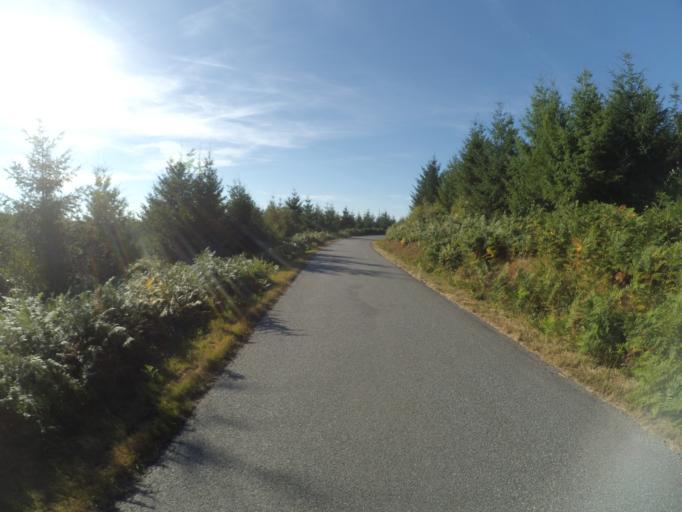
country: FR
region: Limousin
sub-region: Departement de la Creuse
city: Banize
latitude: 45.7738
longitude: 1.9889
